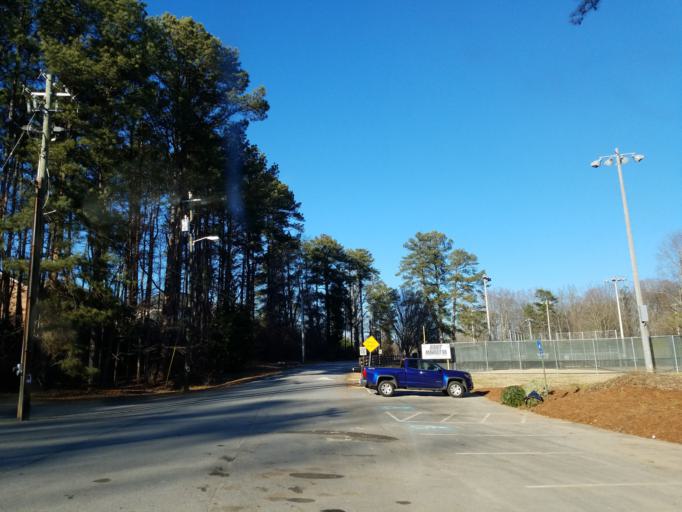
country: US
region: Georgia
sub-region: Cobb County
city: Marietta
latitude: 33.9510
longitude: -84.4921
